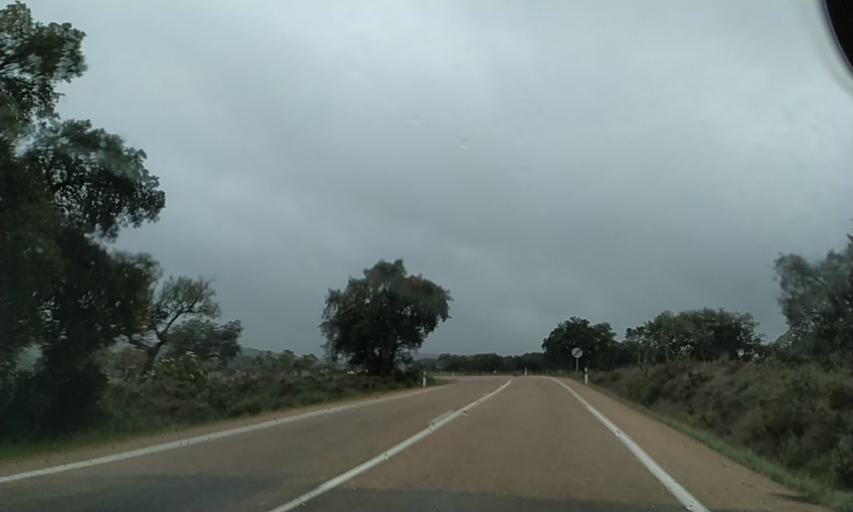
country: ES
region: Extremadura
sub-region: Provincia de Badajoz
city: Puebla de Obando
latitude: 39.2094
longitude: -6.5853
